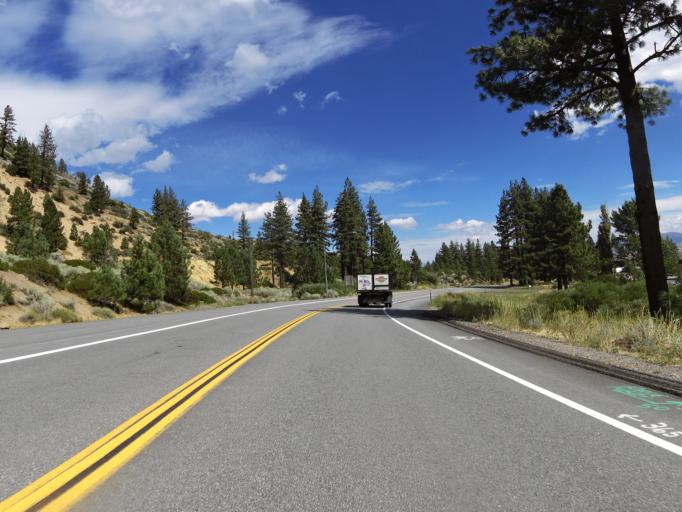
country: US
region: Nevada
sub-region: Douglas County
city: Gardnerville Ranchos
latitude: 38.7731
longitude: -119.8299
